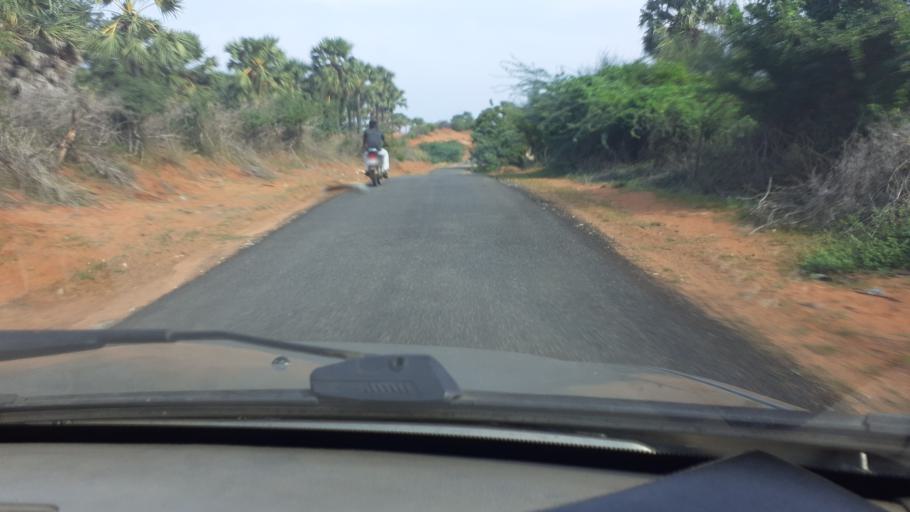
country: IN
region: Tamil Nadu
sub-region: Tirunelveli Kattabo
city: Tisaiyanvilai
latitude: 8.3376
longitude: 77.9462
